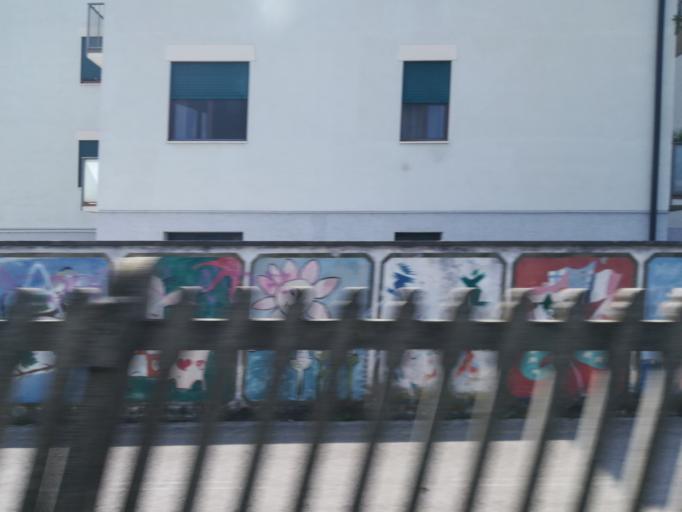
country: IT
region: Veneto
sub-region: Provincia di Vicenza
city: Monticello Conte Otto
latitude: 45.5989
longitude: 11.5700
